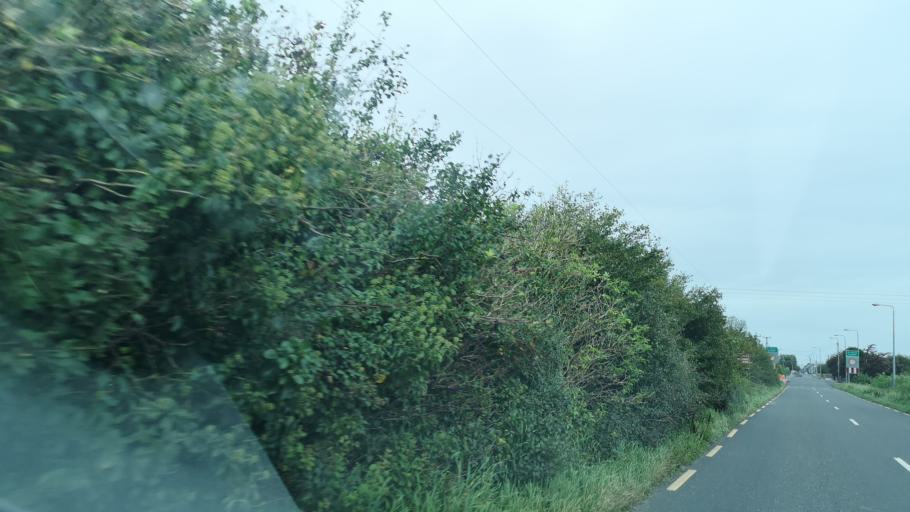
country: IE
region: Leinster
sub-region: Uibh Fhaili
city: Ferbane
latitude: 53.2197
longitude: -7.8914
